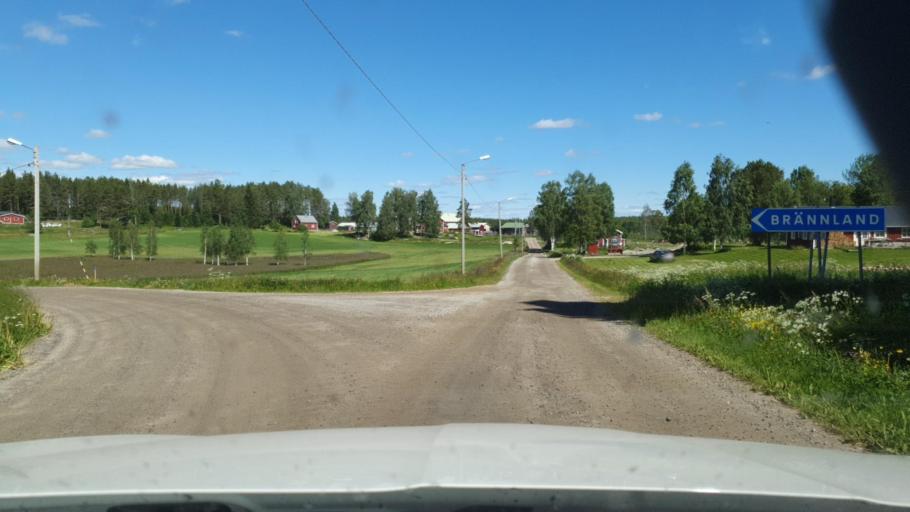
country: SE
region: Vaesterbotten
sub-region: Skelleftea Kommun
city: Byske
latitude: 65.1199
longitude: 21.2111
